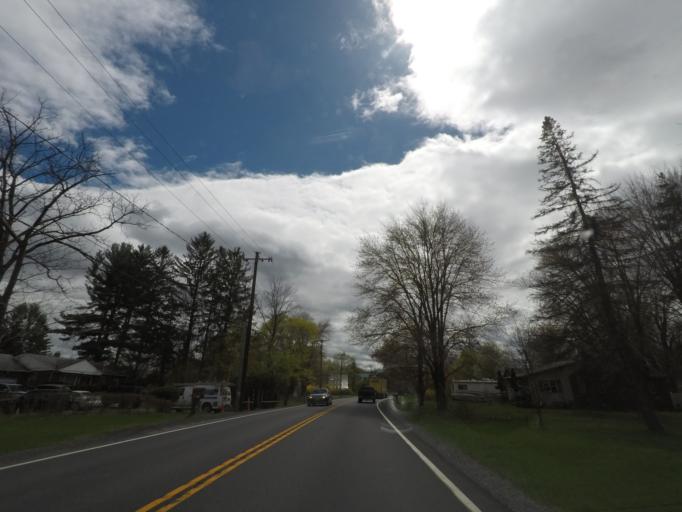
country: US
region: New York
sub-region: Rensselaer County
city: Castleton-on-Hudson
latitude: 42.5083
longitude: -73.7873
